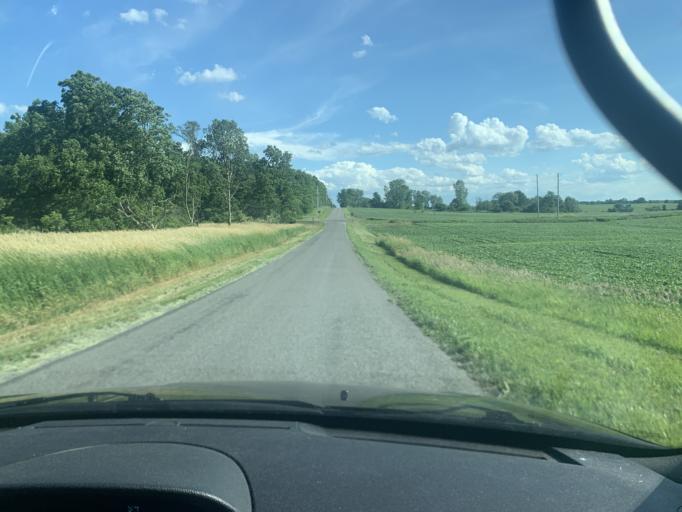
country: US
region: Ohio
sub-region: Logan County
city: De Graff
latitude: 40.3107
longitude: -83.8744
